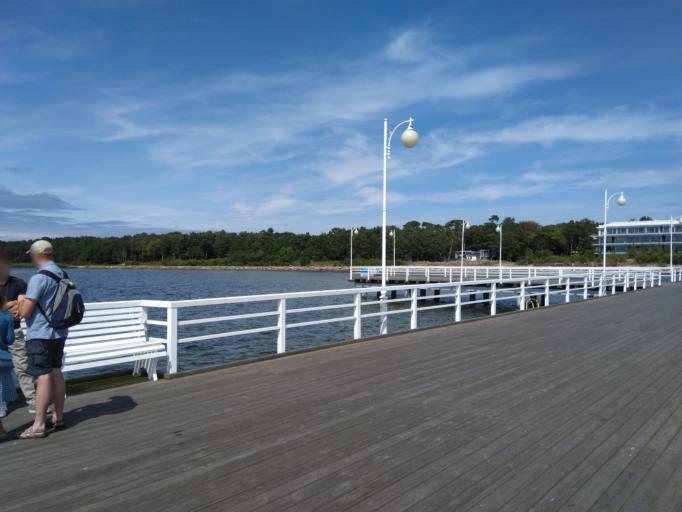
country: PL
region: Pomeranian Voivodeship
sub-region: Powiat pucki
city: Jastarnia
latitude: 54.6810
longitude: 18.7088
